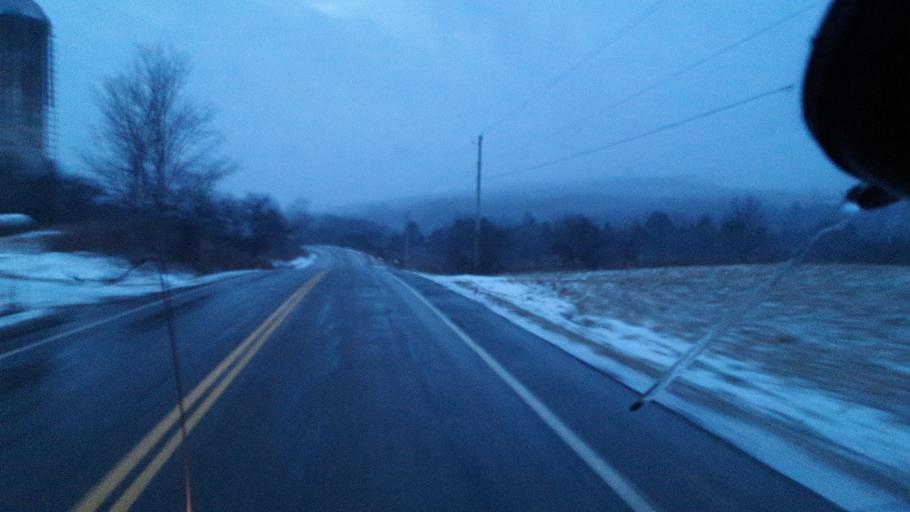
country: US
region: New York
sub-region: Allegany County
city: Houghton
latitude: 42.3244
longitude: -78.1186
